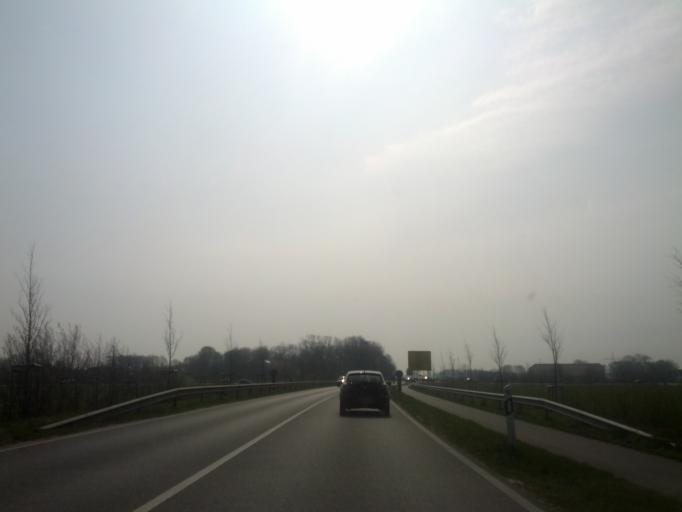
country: DE
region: Lower Saxony
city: Lutetsburg
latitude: 53.6004
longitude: 7.2354
